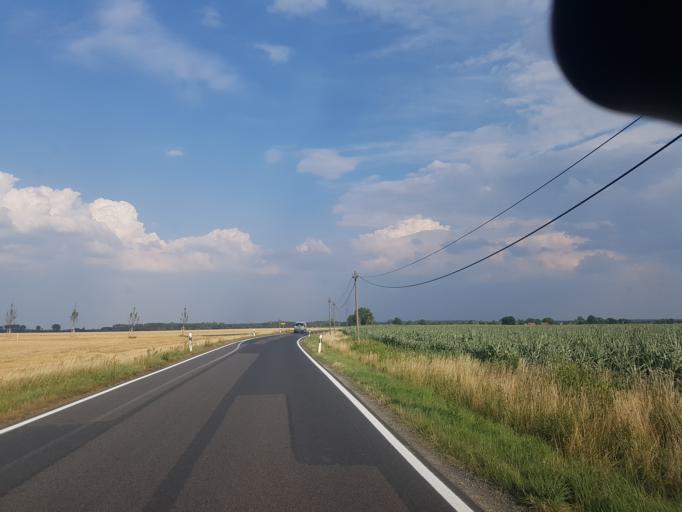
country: DE
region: Brandenburg
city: Herzberg
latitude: 51.6940
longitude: 13.2635
